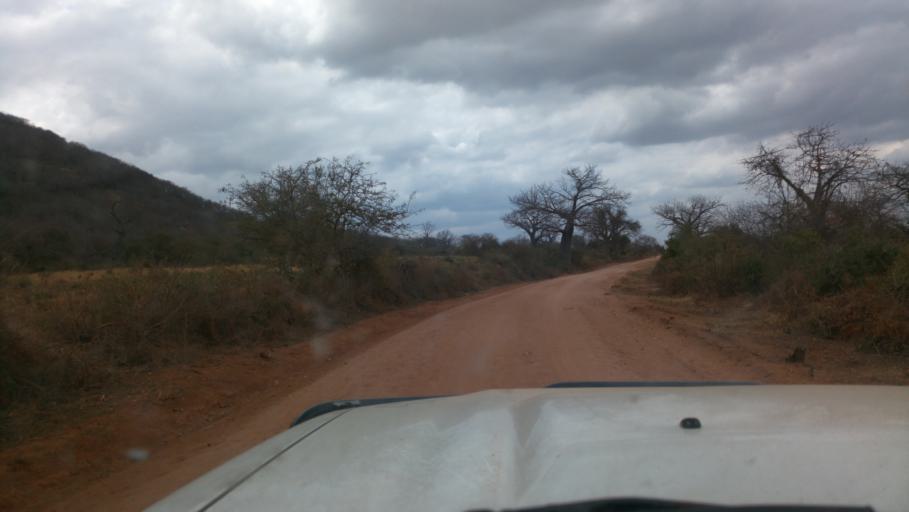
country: KE
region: Kitui
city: Kitui
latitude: -1.8848
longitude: 38.4235
